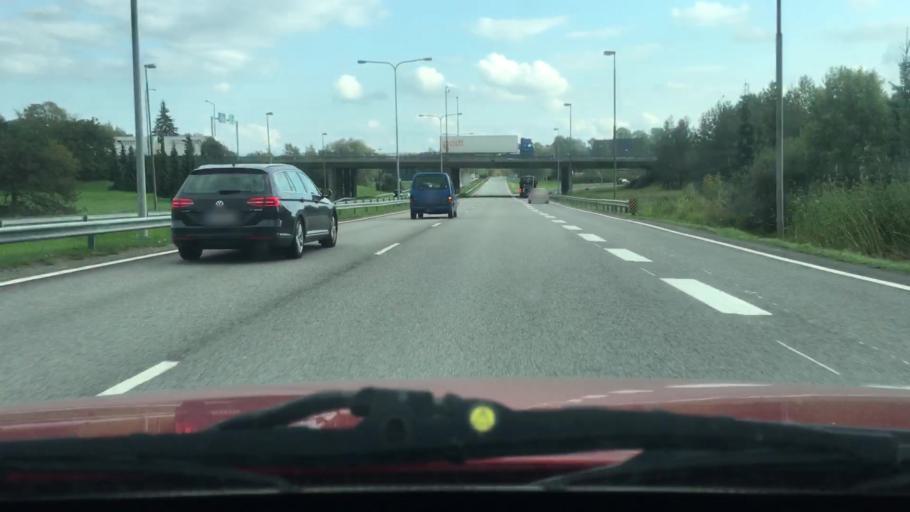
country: FI
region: Varsinais-Suomi
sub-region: Turku
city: Raisio
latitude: 60.4891
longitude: 22.1731
